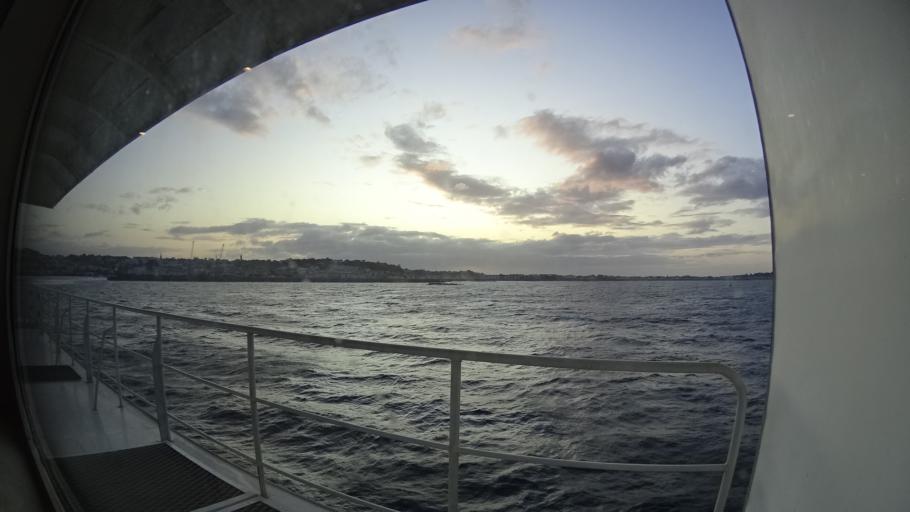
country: GG
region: St Peter Port
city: Saint Peter Port
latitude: 49.4576
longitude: -2.5185
